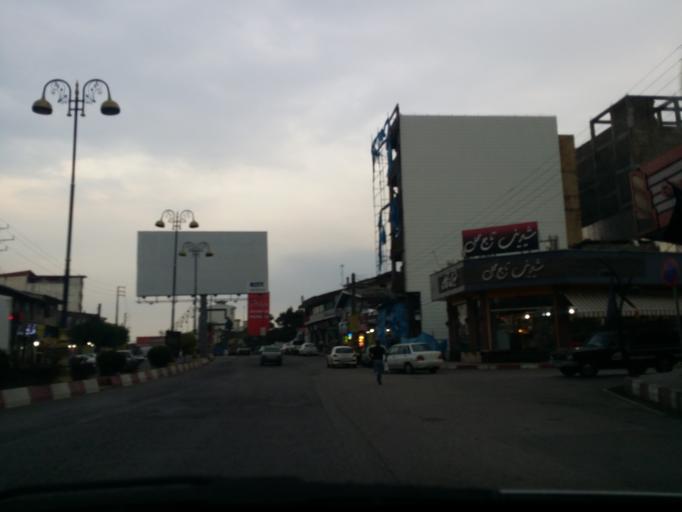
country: IR
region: Mazandaran
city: `Abbasabad
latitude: 36.7281
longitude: 51.1086
